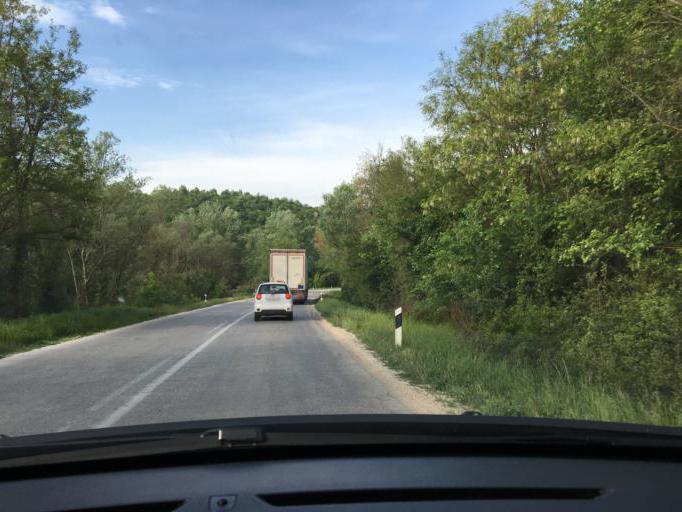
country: MK
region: Kriva Palanka
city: Kriva Palanka
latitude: 42.1749
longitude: 22.2362
